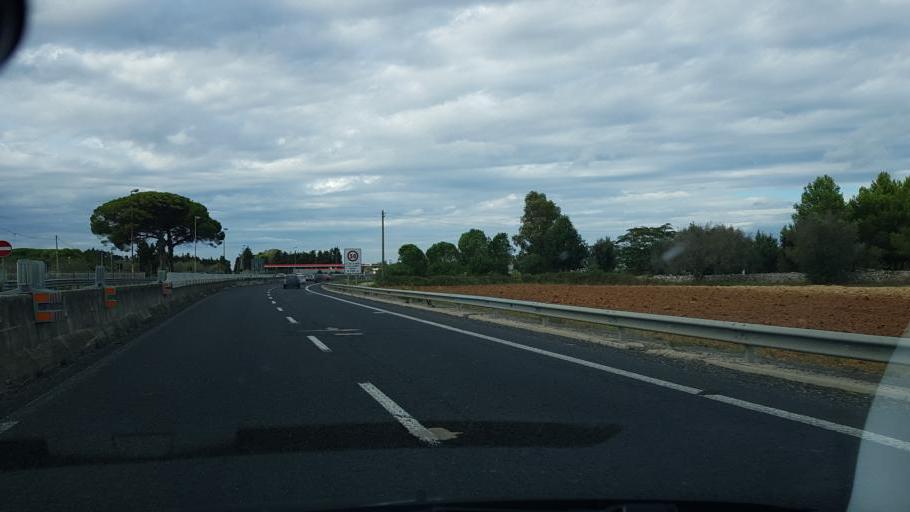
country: IT
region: Apulia
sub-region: Provincia di Lecce
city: Cavallino
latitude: 40.3088
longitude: 18.1900
